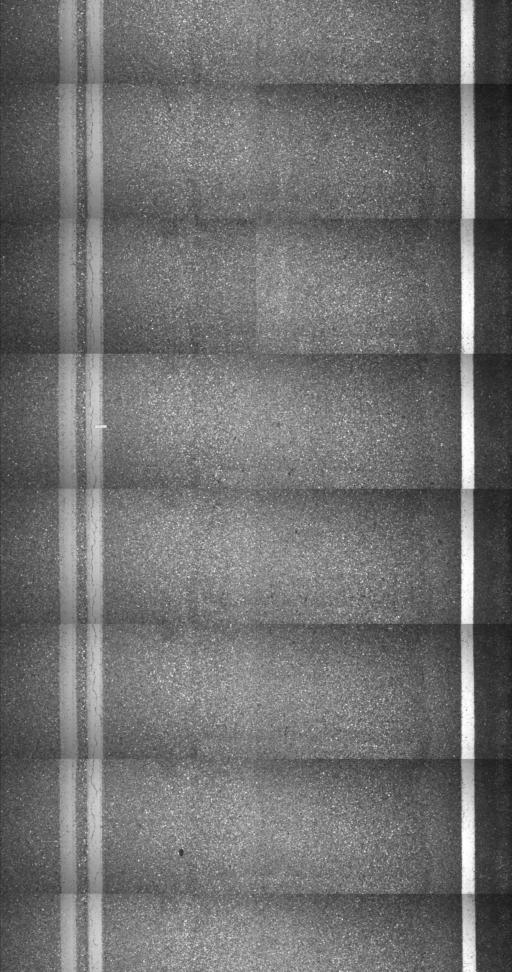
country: US
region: New York
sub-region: Essex County
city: Port Henry
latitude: 44.0234
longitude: -73.3915
